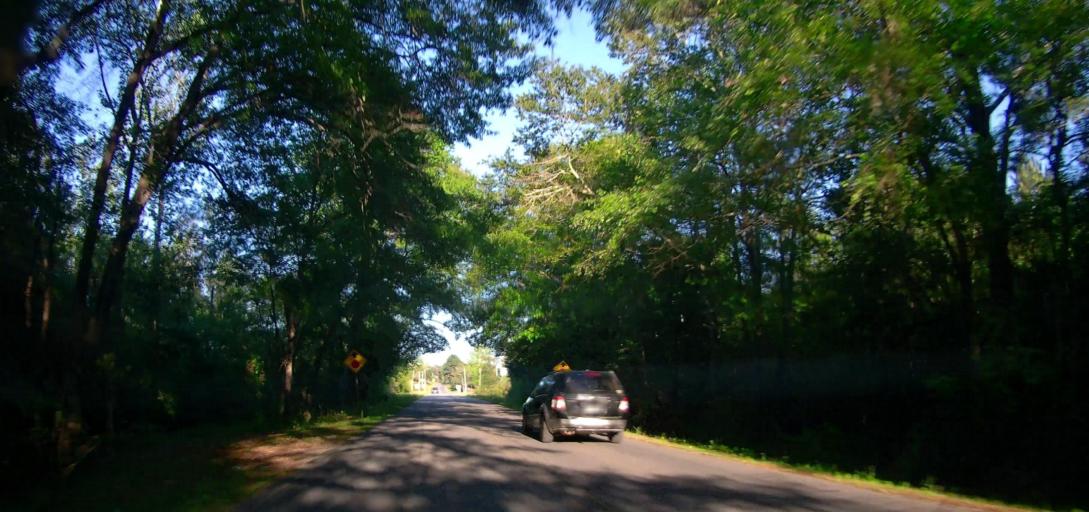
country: US
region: Georgia
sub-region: Ben Hill County
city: Fitzgerald
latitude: 31.7069
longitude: -83.2401
